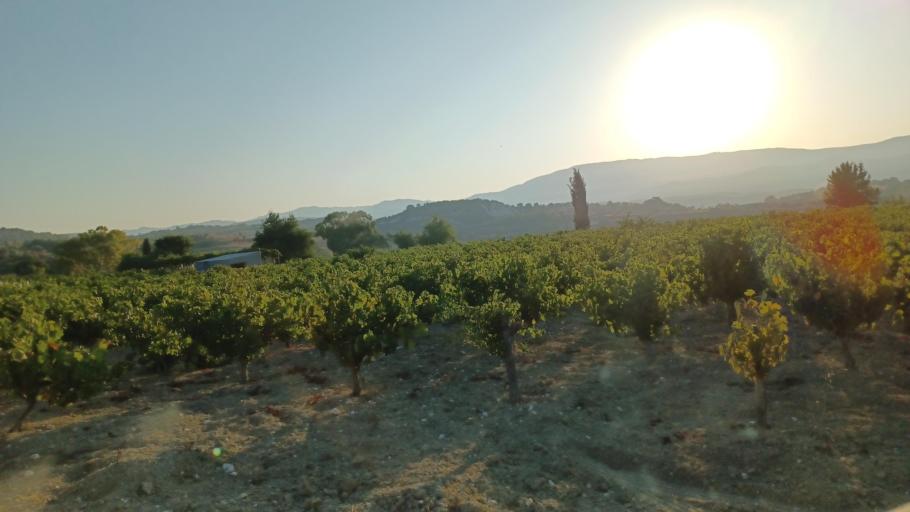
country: CY
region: Pafos
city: Mesogi
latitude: 34.8727
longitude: 32.5099
